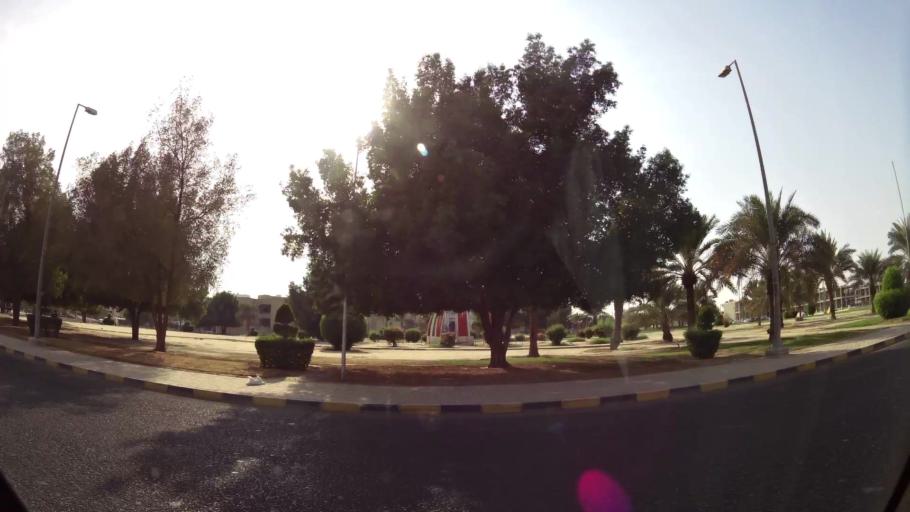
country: KW
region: Al Asimah
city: Ash Shamiyah
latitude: 29.3265
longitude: 47.9820
